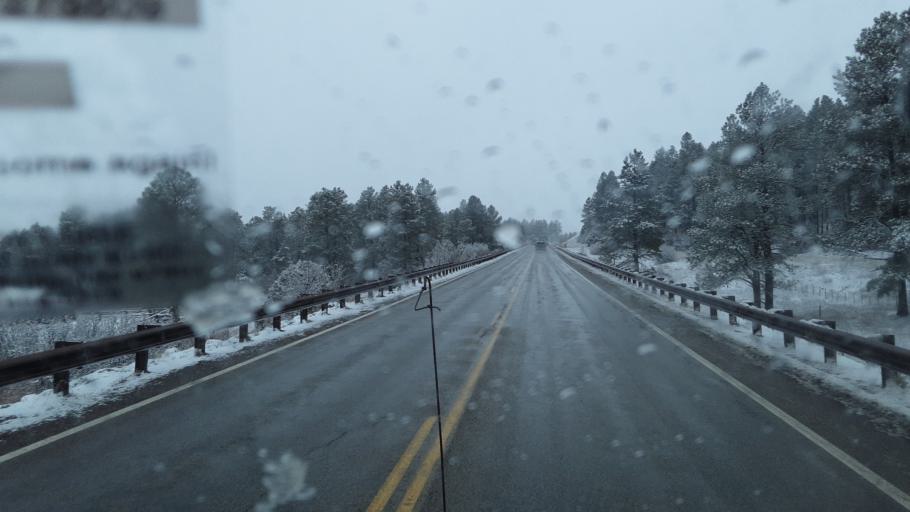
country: US
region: Colorado
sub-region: Archuleta County
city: Pagosa Springs
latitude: 37.2060
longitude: -106.9720
